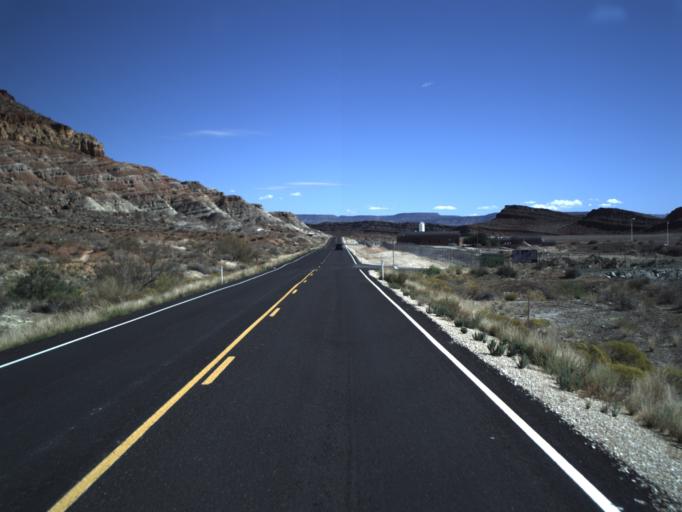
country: US
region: Utah
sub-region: Washington County
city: Washington
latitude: 37.1713
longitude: -113.4054
